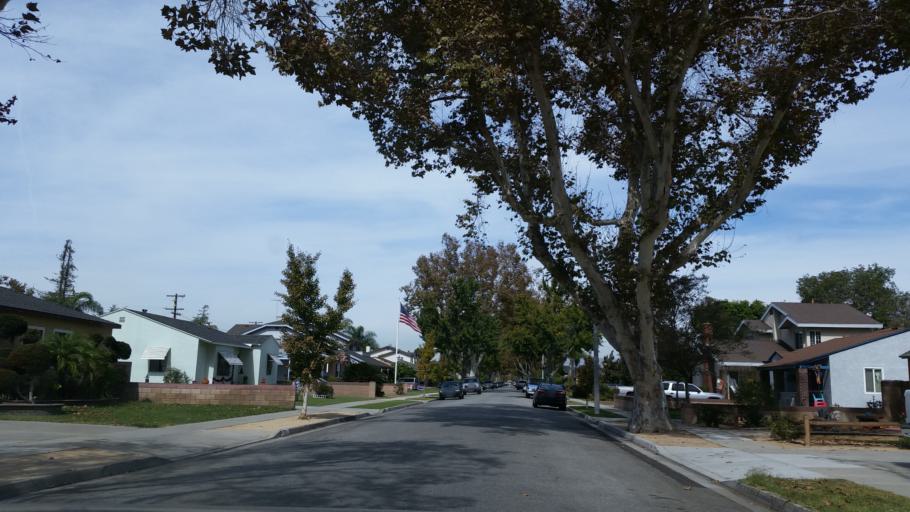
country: US
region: California
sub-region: Los Angeles County
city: Lakewood
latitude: 33.8606
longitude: -118.1281
